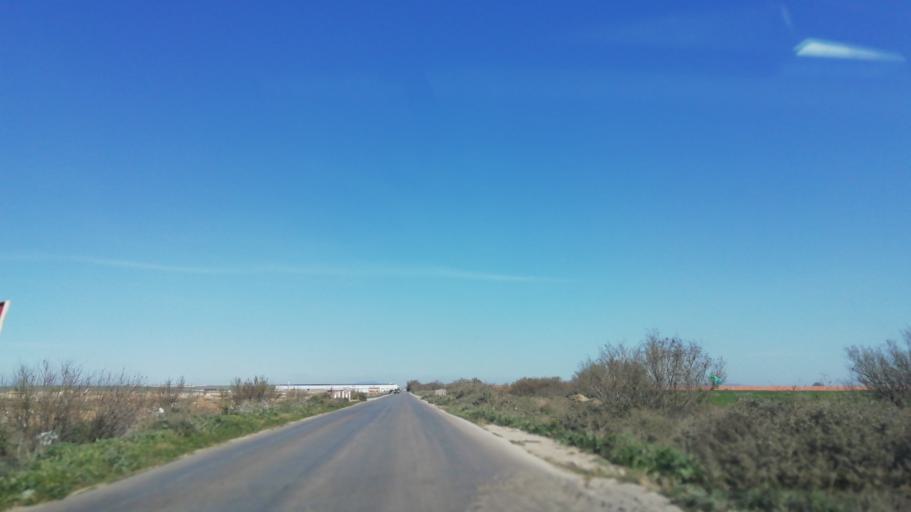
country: DZ
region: Oran
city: Es Senia
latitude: 35.4986
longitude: -0.5961
